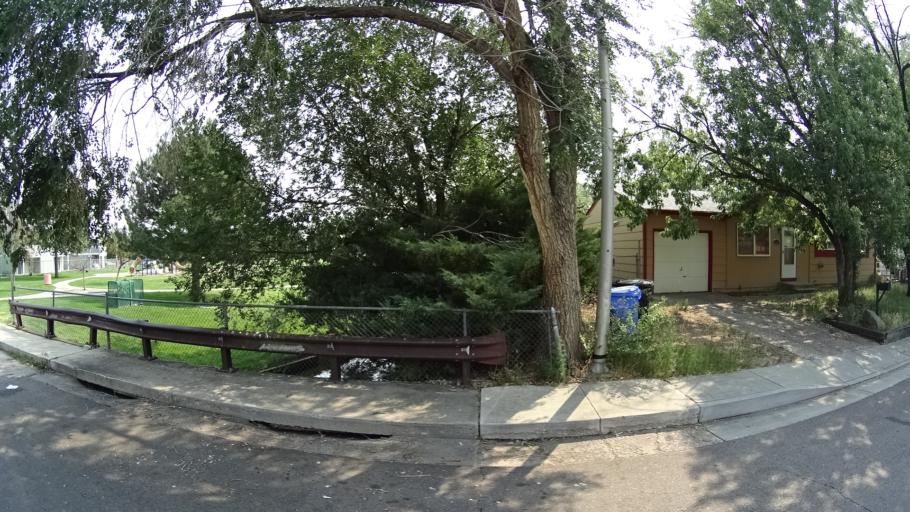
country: US
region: Colorado
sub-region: El Paso County
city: Colorado Springs
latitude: 38.8020
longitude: -104.8135
